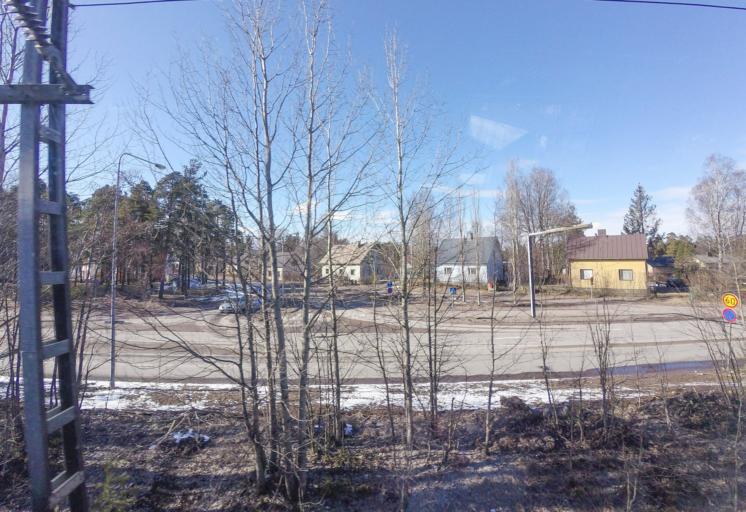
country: FI
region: South Karelia
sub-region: Lappeenranta
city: Lappeenranta
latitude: 61.0726
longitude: 28.2688
